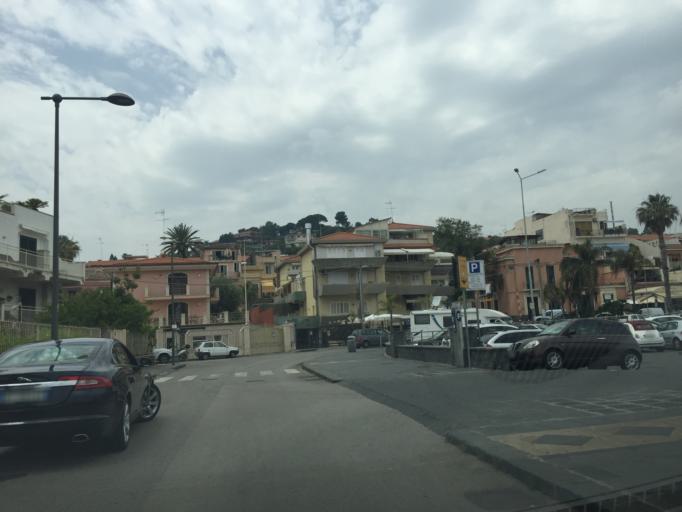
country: IT
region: Sicily
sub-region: Catania
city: Acitrezza
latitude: 37.5613
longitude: 15.1615
